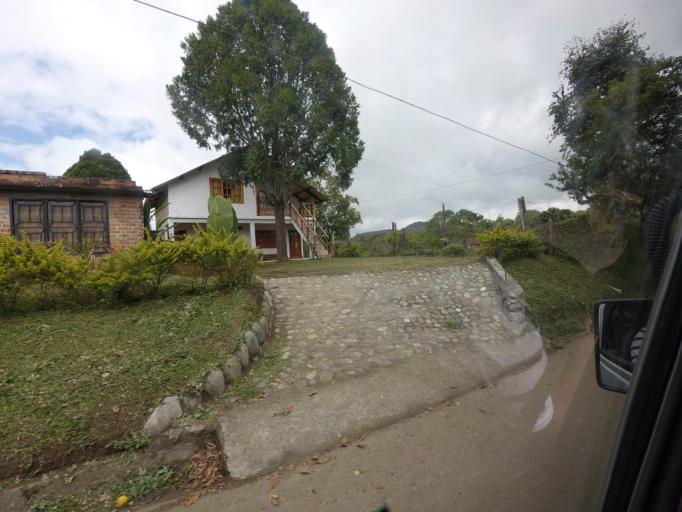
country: CO
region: Huila
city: San Agustin
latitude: 1.8935
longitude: -76.2728
